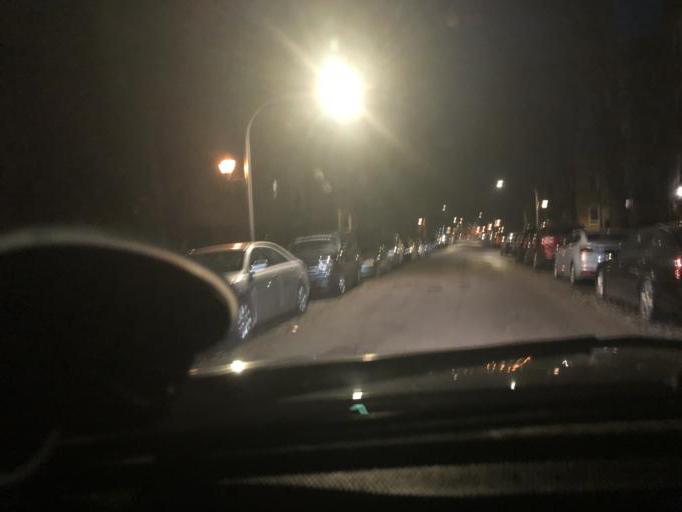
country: US
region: Illinois
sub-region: Cook County
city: Evanston
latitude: 42.0165
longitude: -87.6817
